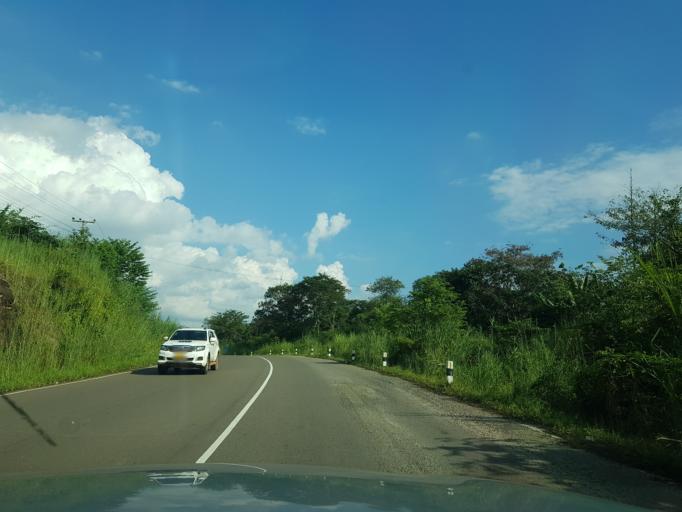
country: TH
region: Nong Khai
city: Pho Tak
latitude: 17.9895
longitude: 102.4272
